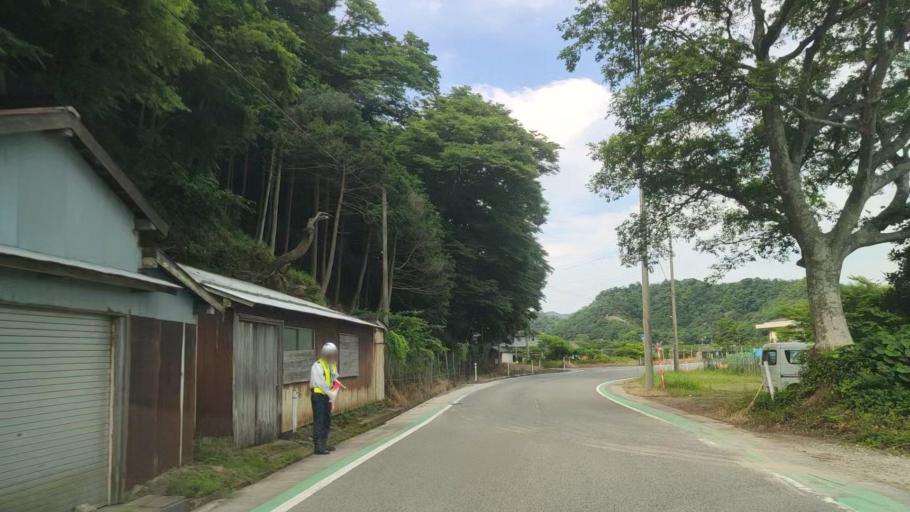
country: JP
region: Hyogo
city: Toyooka
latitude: 35.6414
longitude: 134.8413
